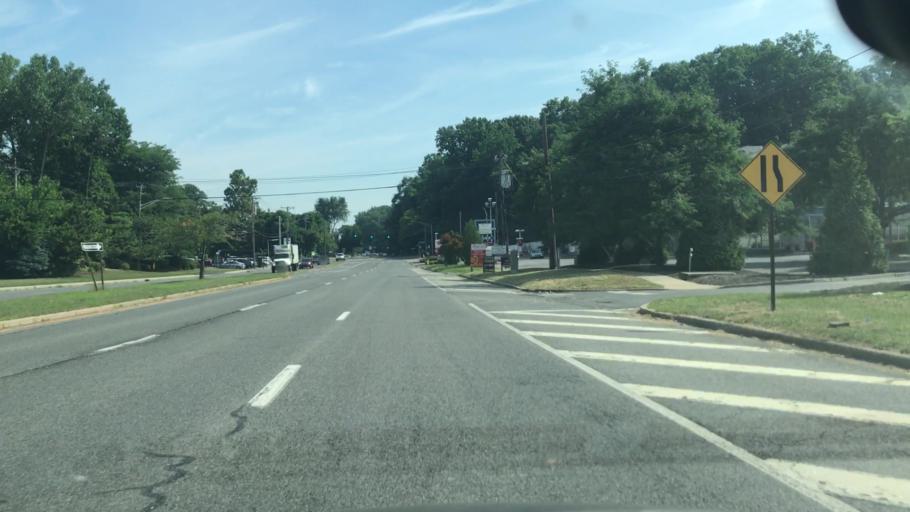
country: US
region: New York
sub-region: Westchester County
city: Greenville
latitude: 40.9864
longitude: -73.8251
